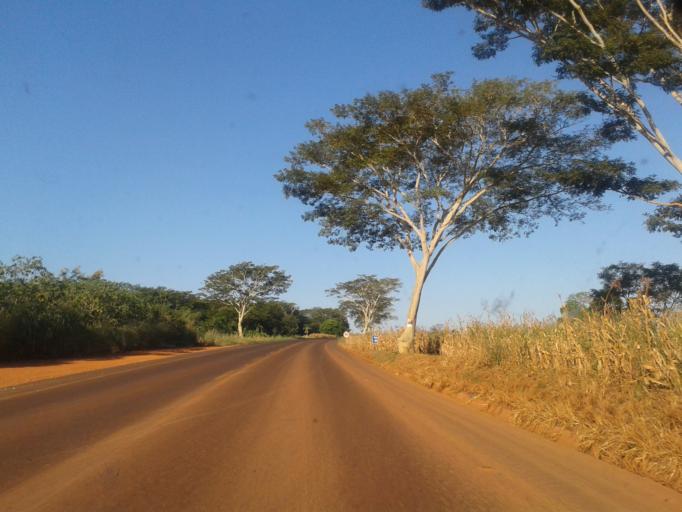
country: BR
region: Minas Gerais
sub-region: Santa Vitoria
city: Santa Vitoria
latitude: -18.6915
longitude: -49.9037
